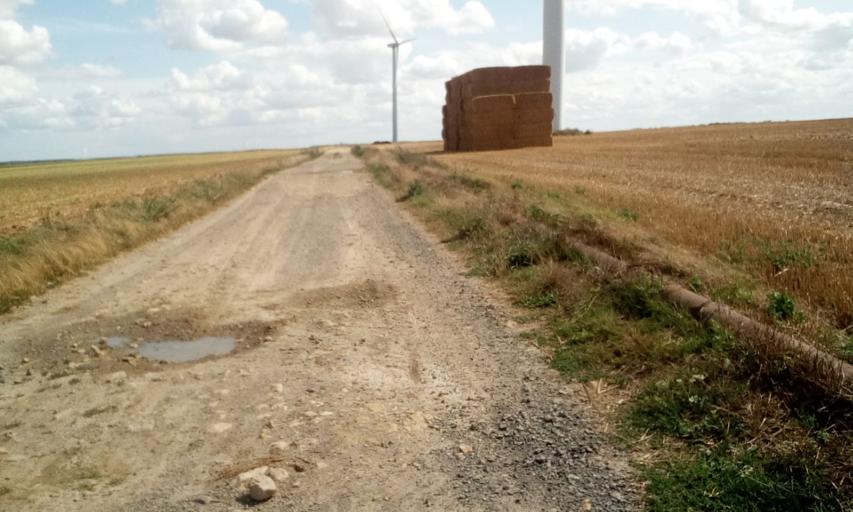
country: FR
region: Lower Normandy
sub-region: Departement du Calvados
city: Bellengreville
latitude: 49.0998
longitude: -0.2298
